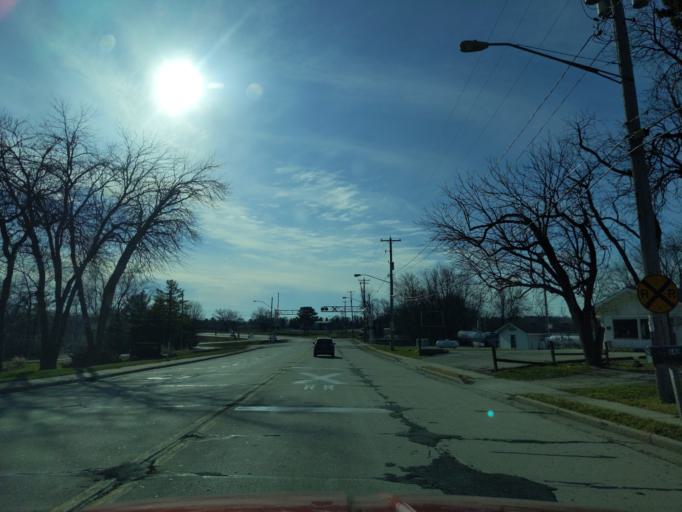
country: US
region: Wisconsin
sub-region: Walworth County
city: Whitewater
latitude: 42.8253
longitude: -88.7445
